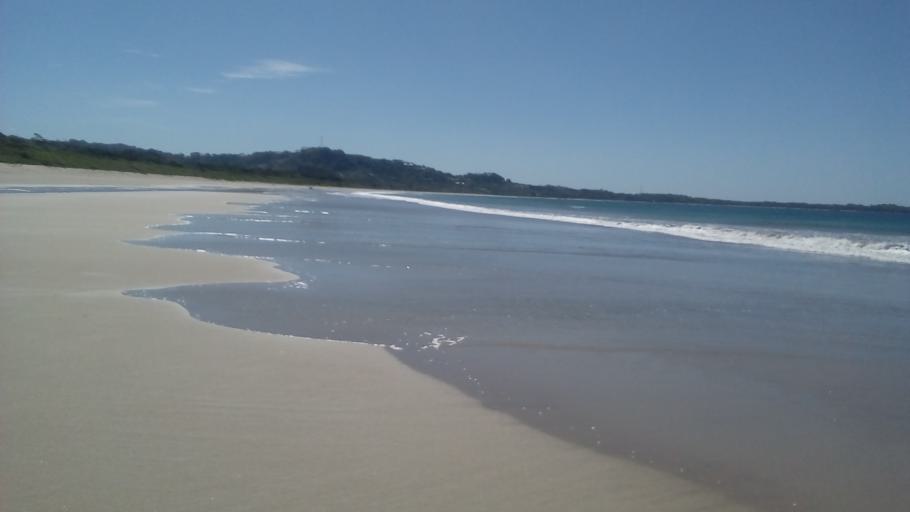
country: CR
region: Guanacaste
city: Santa Cruz
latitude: 10.3276
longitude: -85.8444
